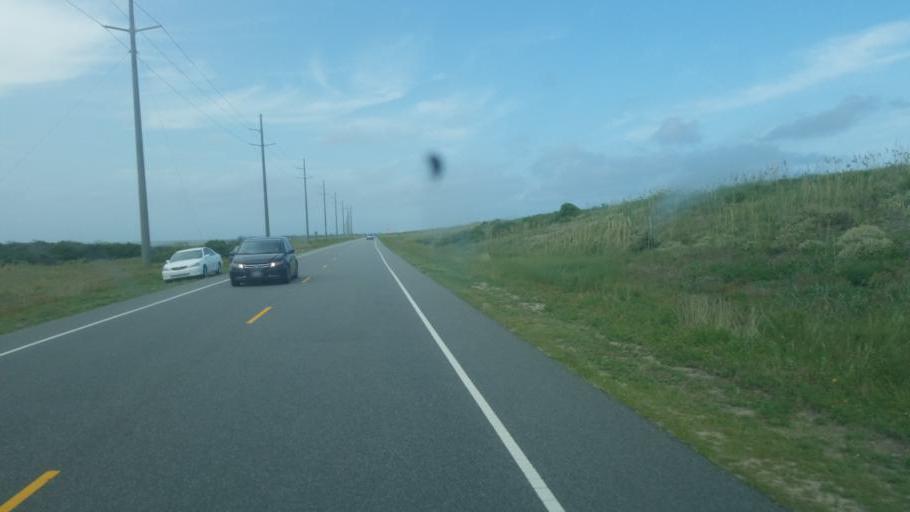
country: US
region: North Carolina
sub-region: Dare County
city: Buxton
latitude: 35.2865
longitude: -75.5160
